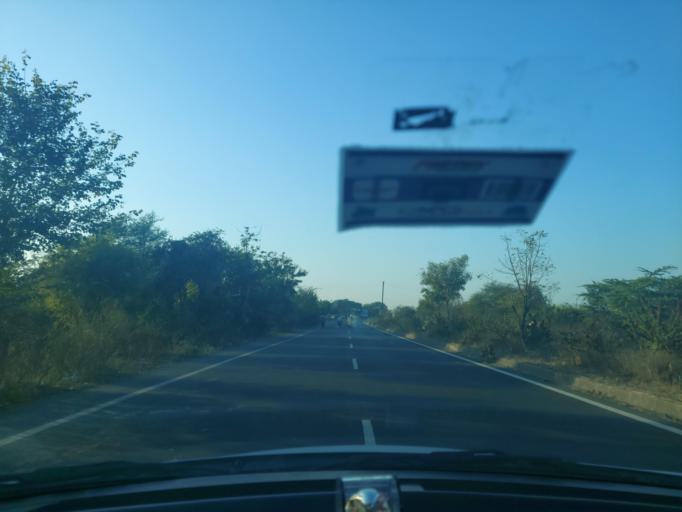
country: IN
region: Madhya Pradesh
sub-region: Indore
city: Sanwer
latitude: 23.0488
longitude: 75.8276
